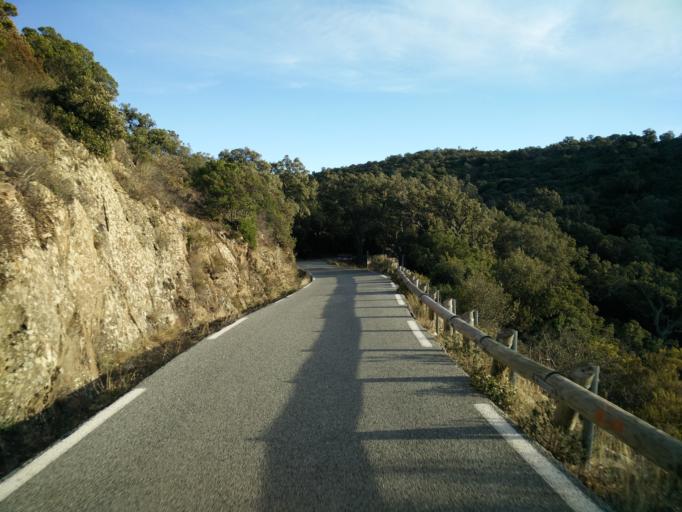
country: FR
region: Provence-Alpes-Cote d'Azur
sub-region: Departement du Var
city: Bormes-les-Mimosas
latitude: 43.1886
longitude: 6.3236
